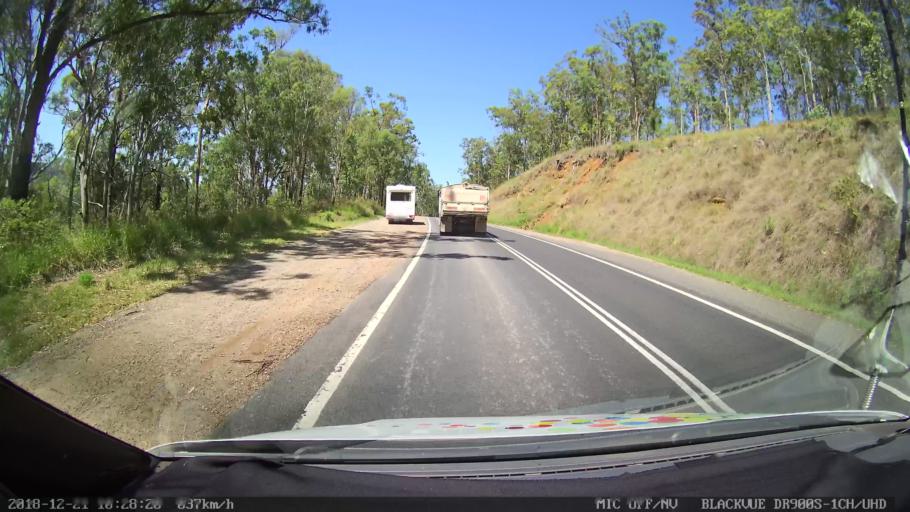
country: AU
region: New South Wales
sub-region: Clarence Valley
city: South Grafton
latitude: -29.6305
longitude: 152.7349
